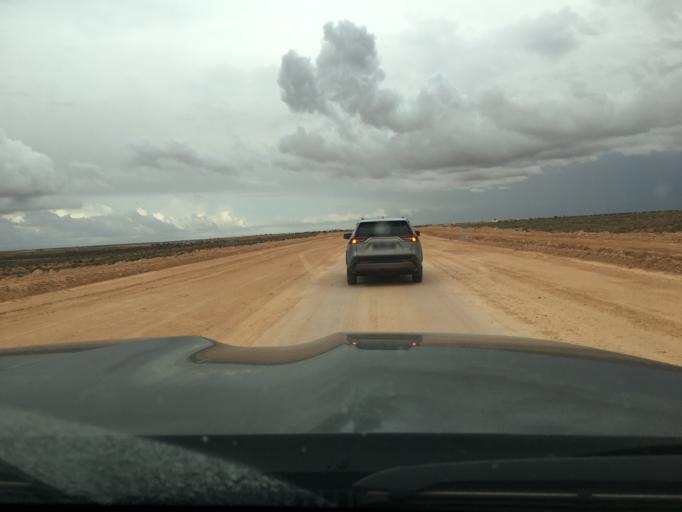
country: TN
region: Madanin
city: Medenine
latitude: 33.2816
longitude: 10.5955
